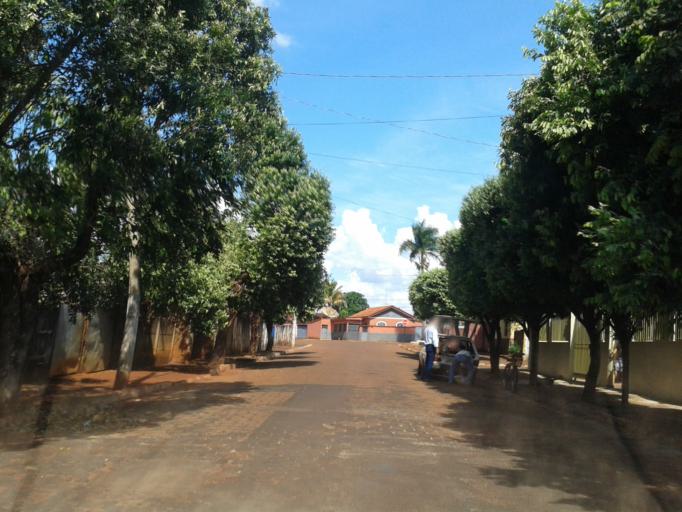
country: BR
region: Minas Gerais
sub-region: Centralina
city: Centralina
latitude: -18.5893
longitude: -49.1981
